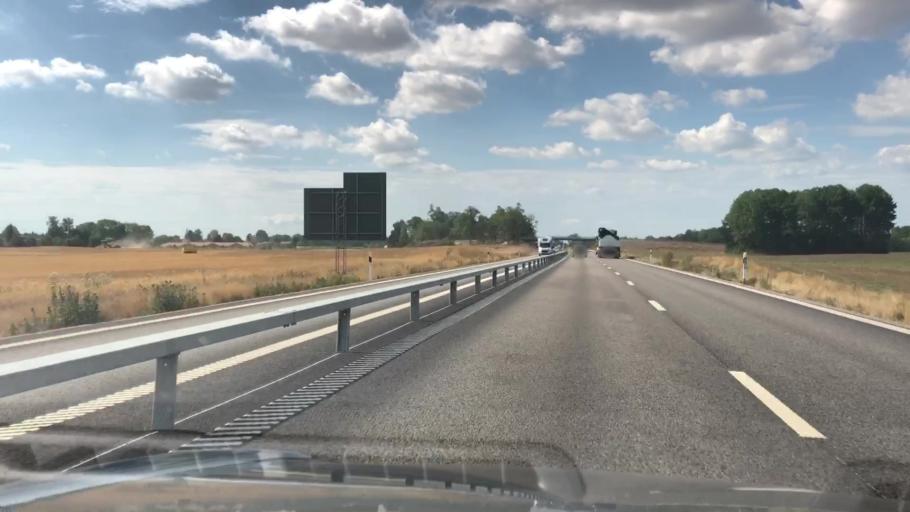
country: SE
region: Kalmar
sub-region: Kalmar Kommun
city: Rinkabyholm
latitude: 56.6587
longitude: 16.2515
